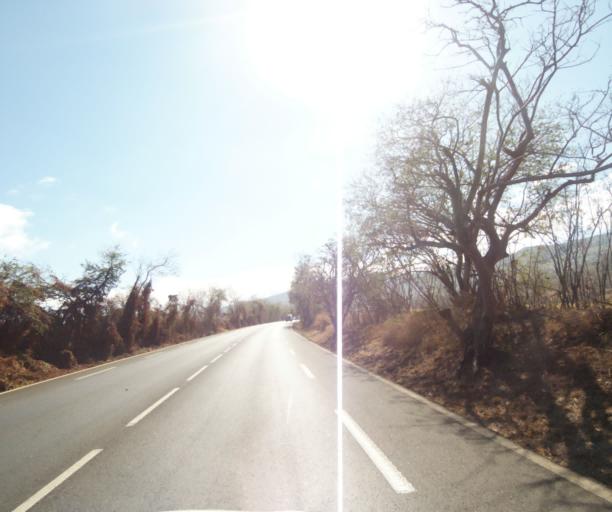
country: RE
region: Reunion
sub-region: Reunion
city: Saint-Paul
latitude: -20.9831
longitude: 55.3035
